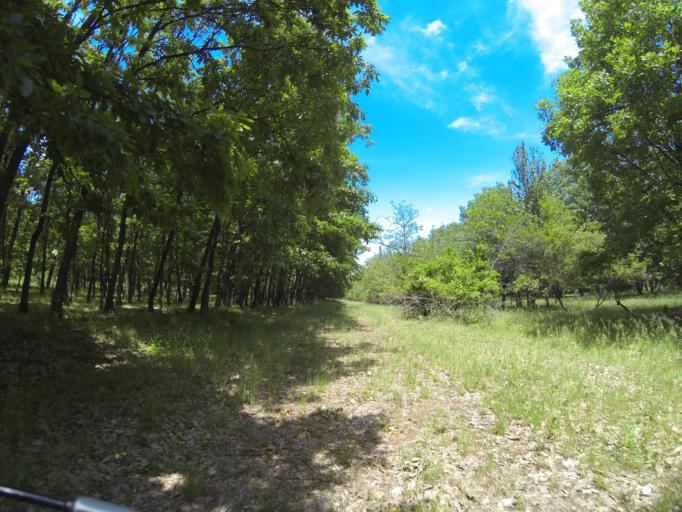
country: RO
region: Dolj
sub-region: Comuna Teslui
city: Teslui
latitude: 44.1677
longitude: 24.1648
